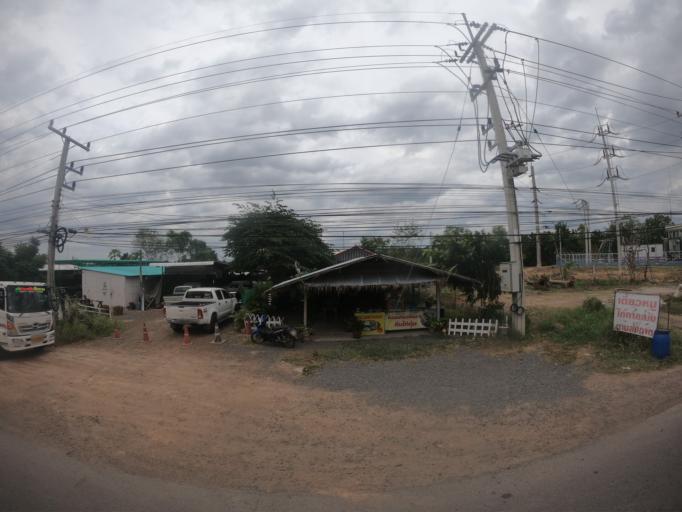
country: TH
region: Nakhon Ratchasima
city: Chok Chai
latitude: 14.8285
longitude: 102.1824
